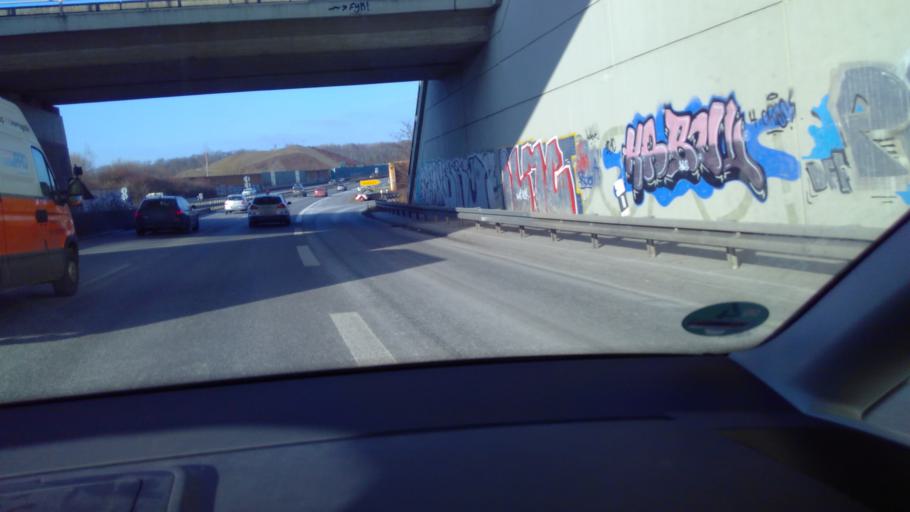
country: DE
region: North Rhine-Westphalia
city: Schwerte
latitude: 51.4838
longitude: 7.5285
